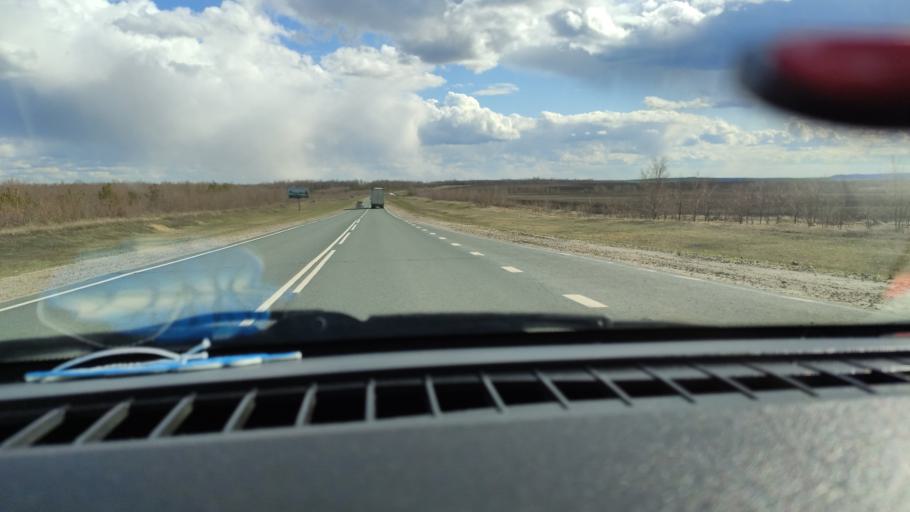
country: RU
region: Saratov
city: Alekseyevka
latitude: 52.2838
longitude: 47.9312
